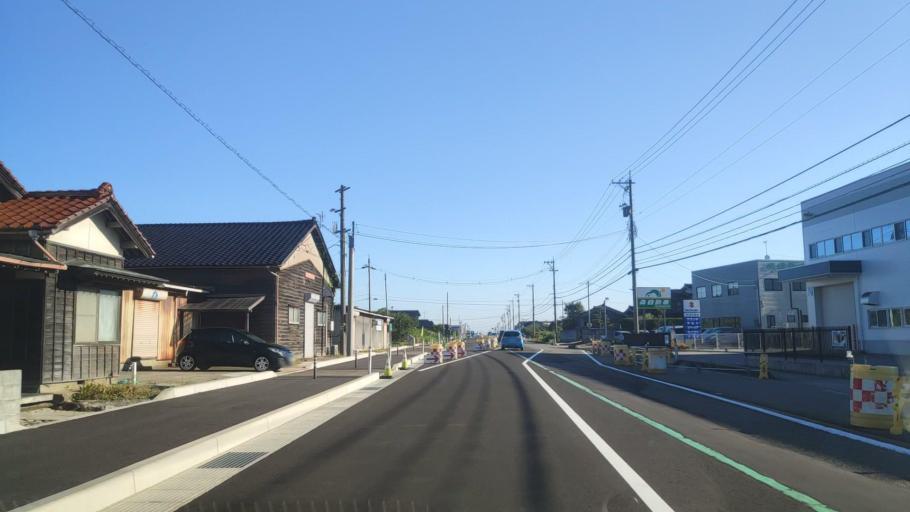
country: JP
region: Ishikawa
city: Tsubata
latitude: 36.7388
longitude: 136.7046
